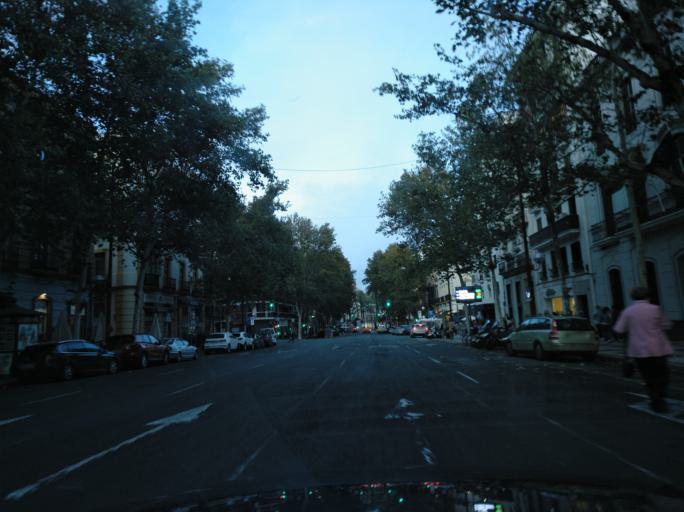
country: ES
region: Andalusia
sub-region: Provincia de Sevilla
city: Sevilla
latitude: 37.3879
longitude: -6.0010
